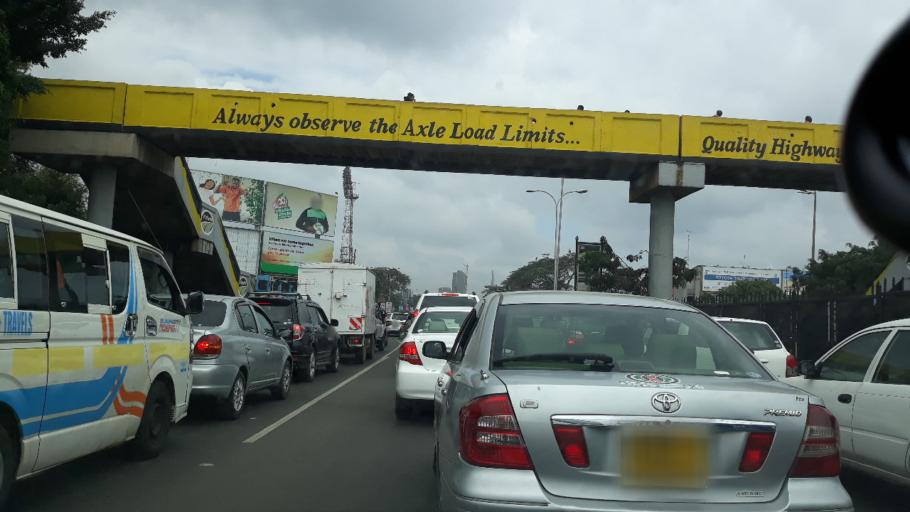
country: KE
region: Nairobi Area
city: Nairobi
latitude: -1.3057
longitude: 36.8268
